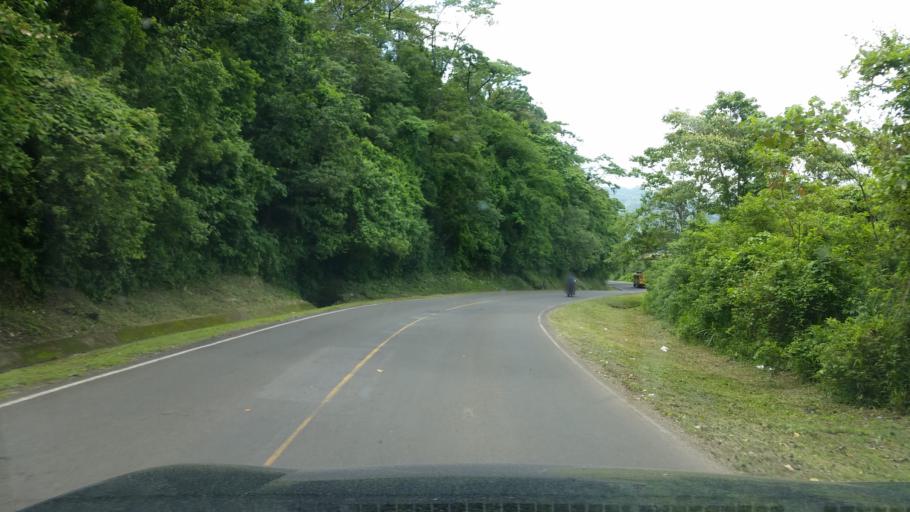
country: NI
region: Matagalpa
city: San Ramon
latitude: 12.9711
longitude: -85.8503
